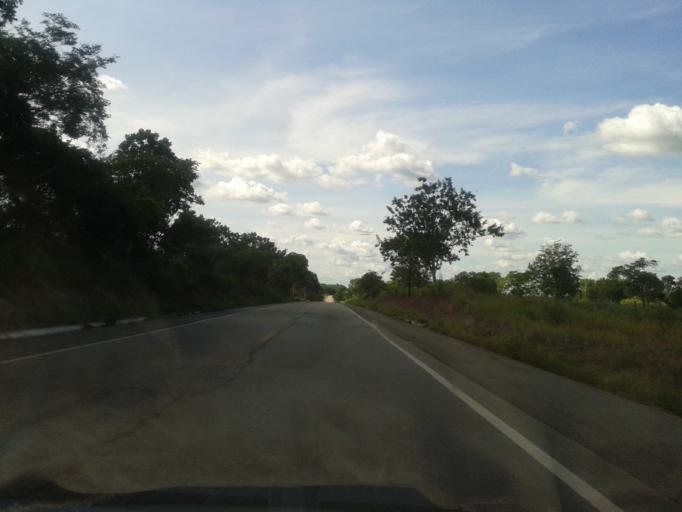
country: BR
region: Goias
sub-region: Mozarlandia
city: Mozarlandia
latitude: -15.2241
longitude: -50.5254
